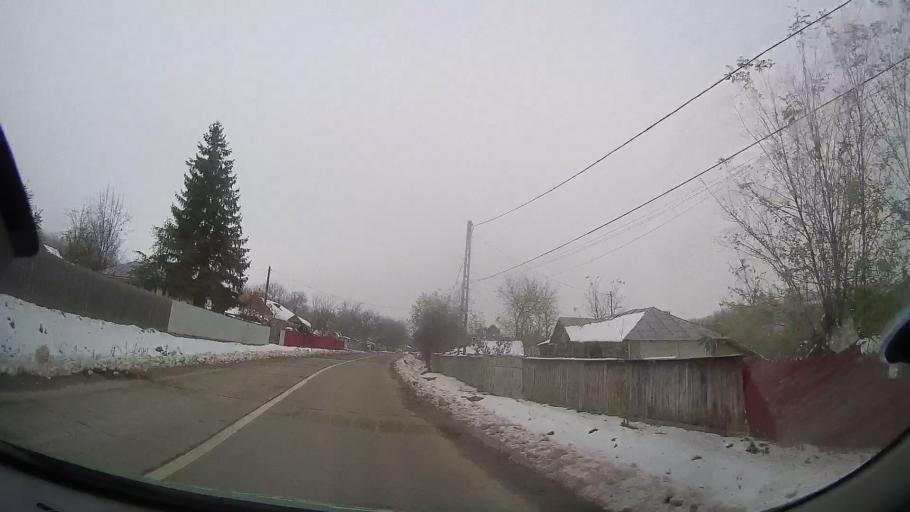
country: RO
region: Vrancea
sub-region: Comuna Boghesti
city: Boghesti
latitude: 46.2011
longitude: 27.4420
